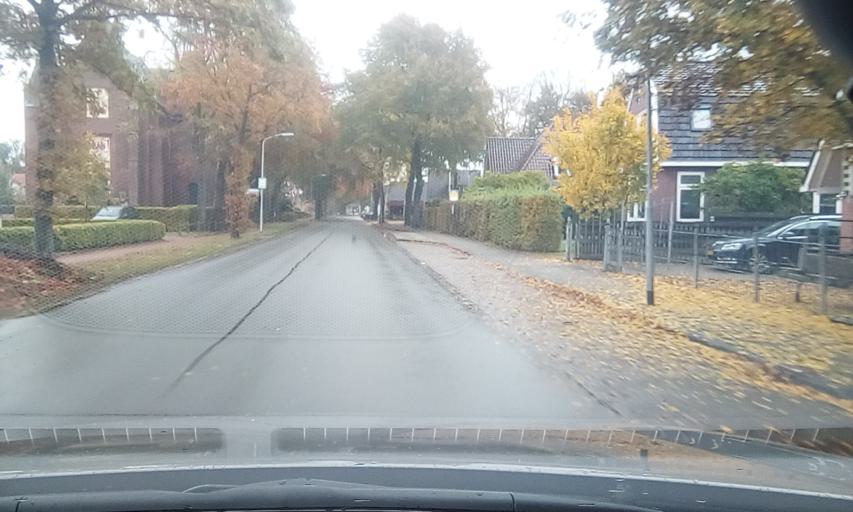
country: NL
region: Groningen
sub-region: Gemeente Hoogezand-Sappemeer
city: Hoogezand
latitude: 53.2125
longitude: 6.6934
